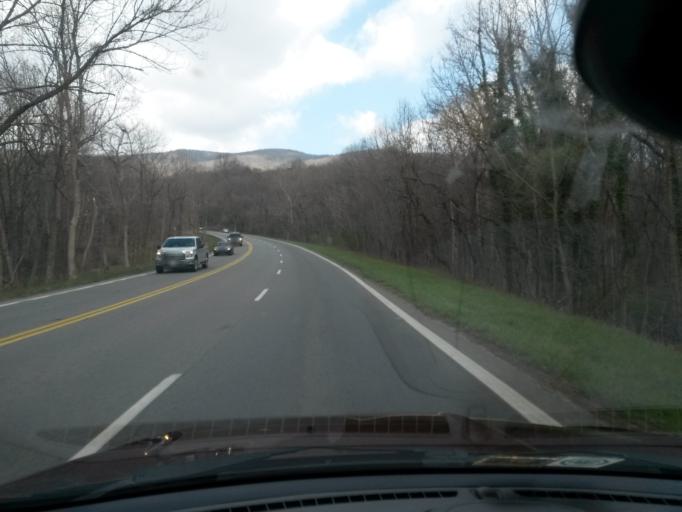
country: US
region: Virginia
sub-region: City of Waynesboro
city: Waynesboro
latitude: 38.0360
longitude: -78.8133
